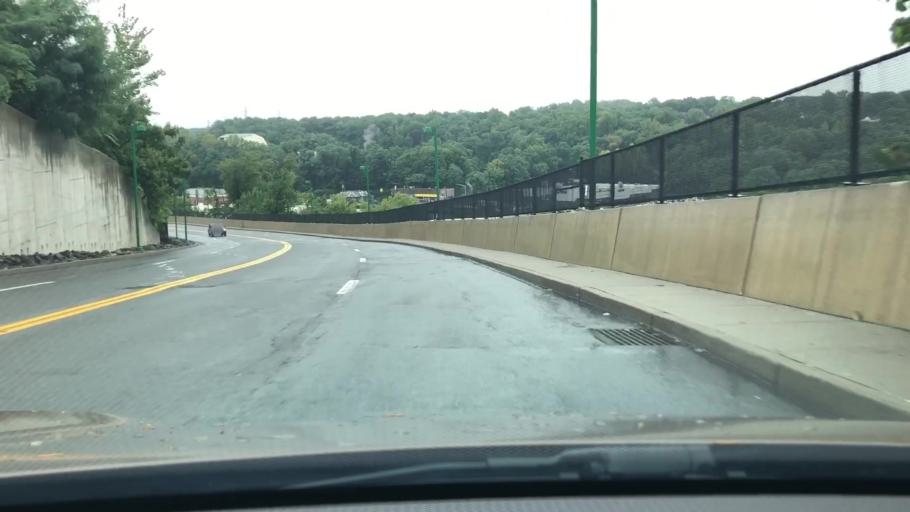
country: US
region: New York
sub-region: Westchester County
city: Tuckahoe
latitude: 40.9572
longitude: -73.8579
